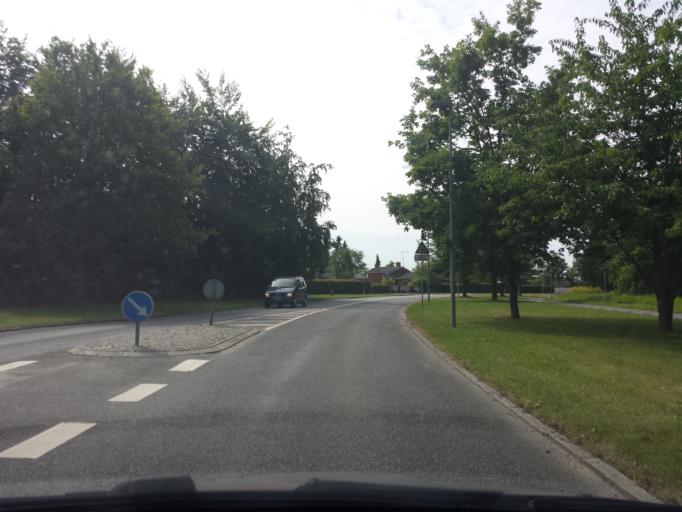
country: DK
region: Capital Region
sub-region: Ballerup Kommune
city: Ballerup
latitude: 55.7187
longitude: 12.3918
